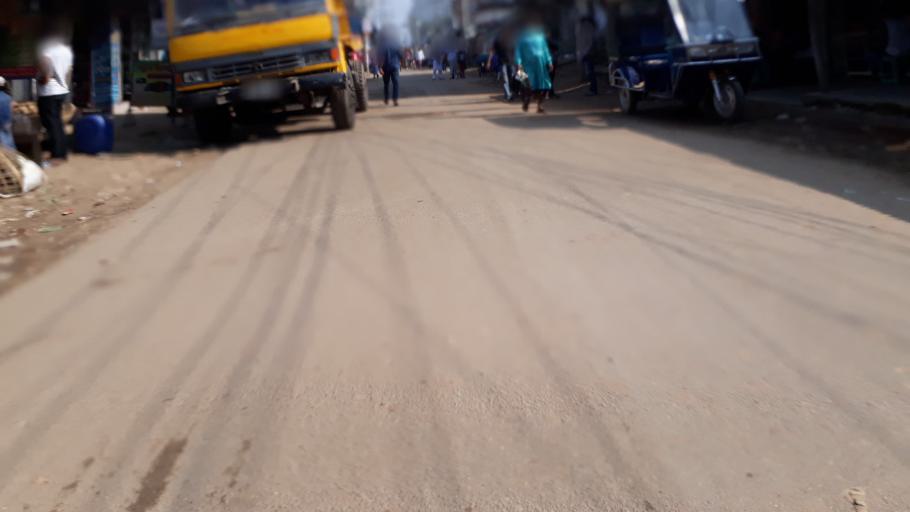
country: BD
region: Dhaka
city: Tungi
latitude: 23.8499
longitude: 90.2825
